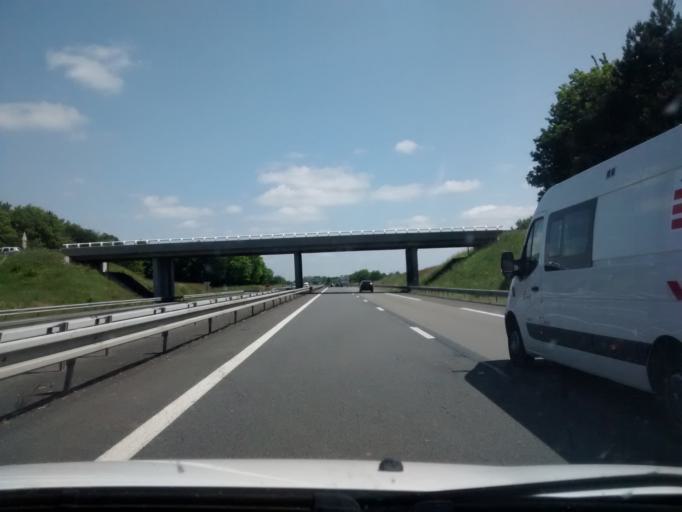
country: FR
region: Pays de la Loire
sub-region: Departement de la Sarthe
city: Brulon
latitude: 48.0060
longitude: -0.2151
